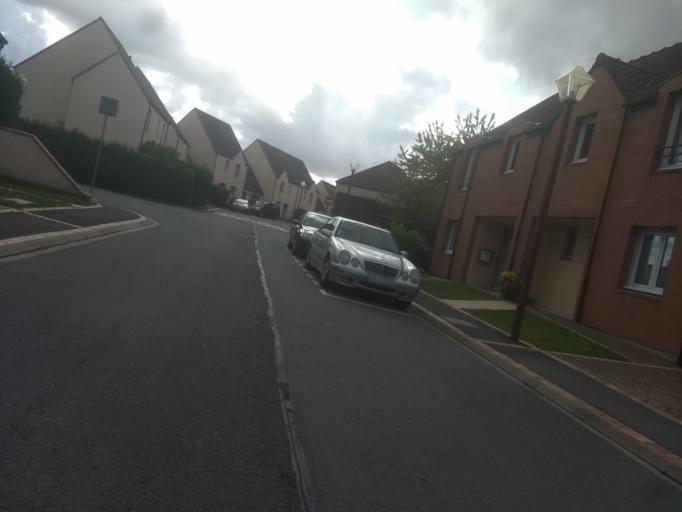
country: FR
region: Nord-Pas-de-Calais
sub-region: Departement du Pas-de-Calais
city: Saint-Laurent-Blangy
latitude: 50.2857
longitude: 2.8019
